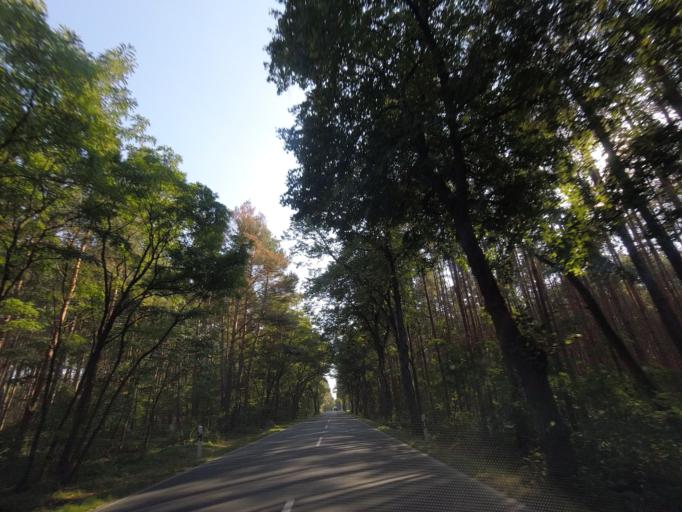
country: DE
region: Saxony-Anhalt
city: Jessen
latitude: 51.8148
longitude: 13.0118
